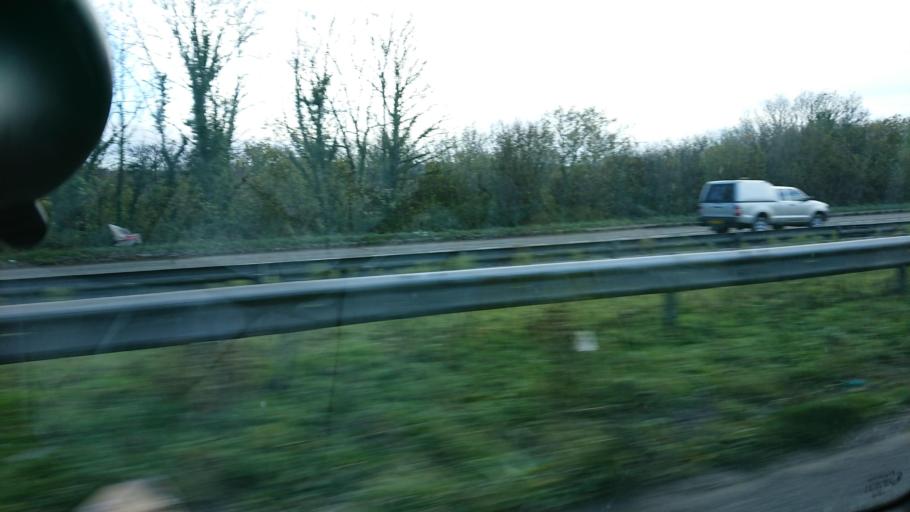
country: GB
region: England
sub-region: Devon
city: Yealmpton
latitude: 50.3815
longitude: -3.9994
